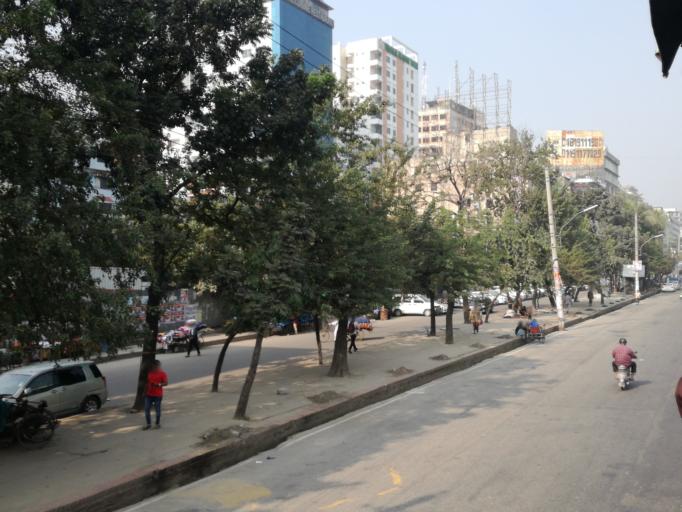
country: BD
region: Dhaka
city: Tungi
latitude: 23.8630
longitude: 90.3998
